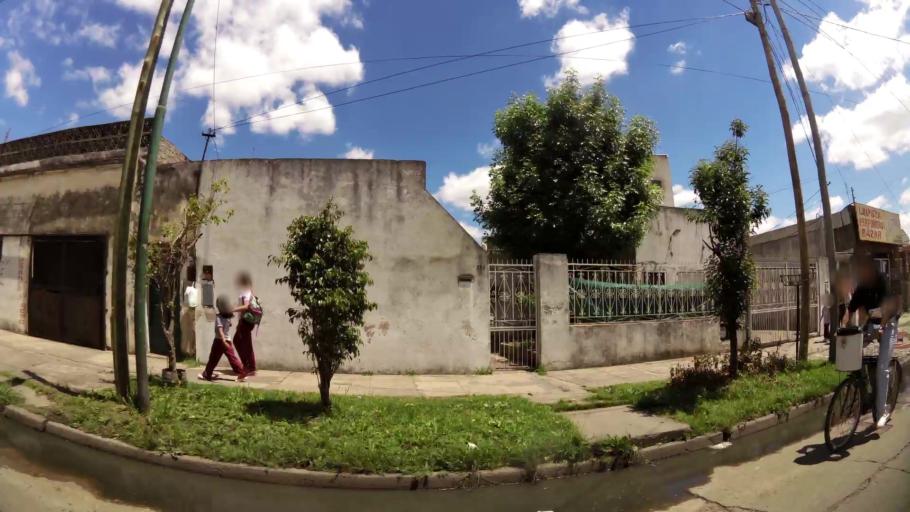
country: AR
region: Buenos Aires
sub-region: Partido de Lanus
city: Lanus
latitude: -34.7193
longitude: -58.4303
